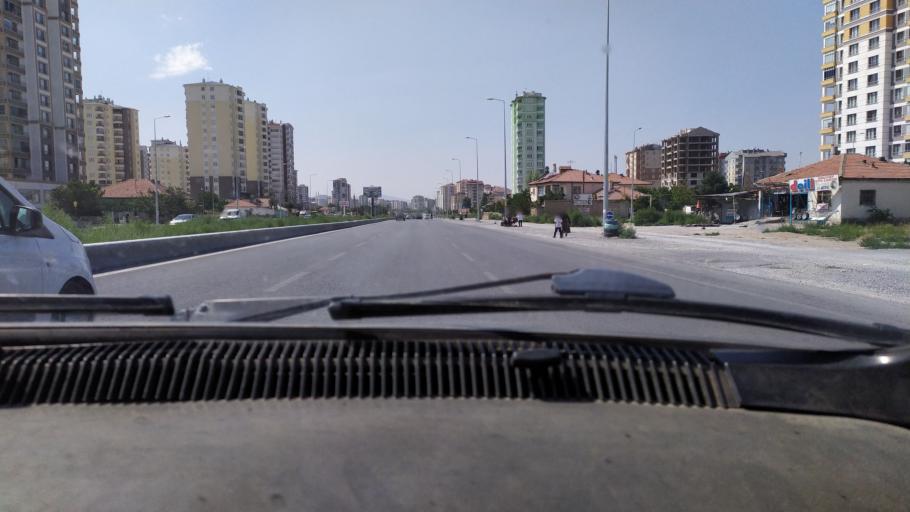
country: TR
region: Kayseri
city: Talas
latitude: 38.7205
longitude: 35.5443
